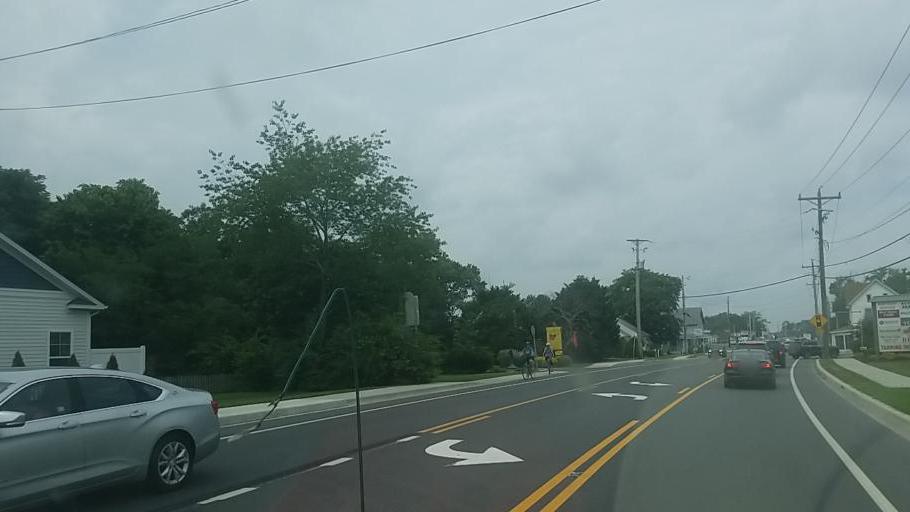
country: US
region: Delaware
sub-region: Sussex County
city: Ocean View
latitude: 38.5434
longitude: -75.0862
